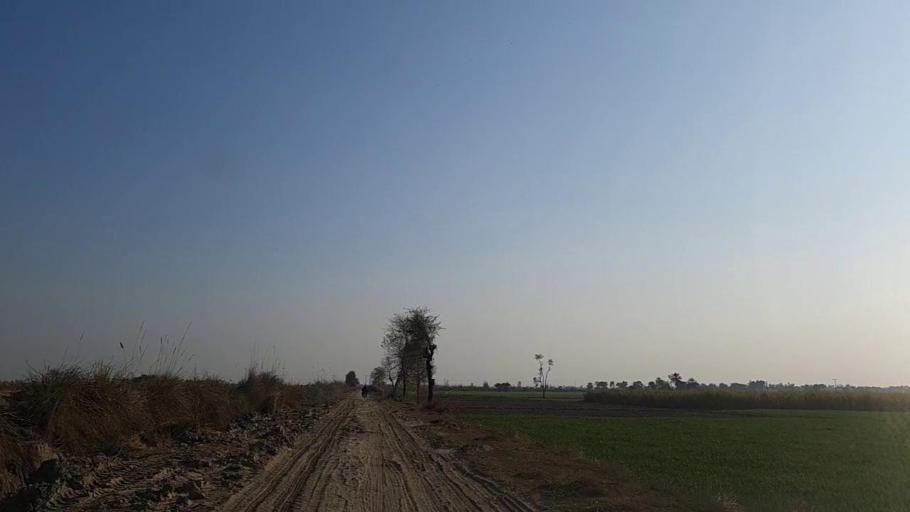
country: PK
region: Sindh
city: Daur
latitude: 26.4399
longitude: 68.3516
